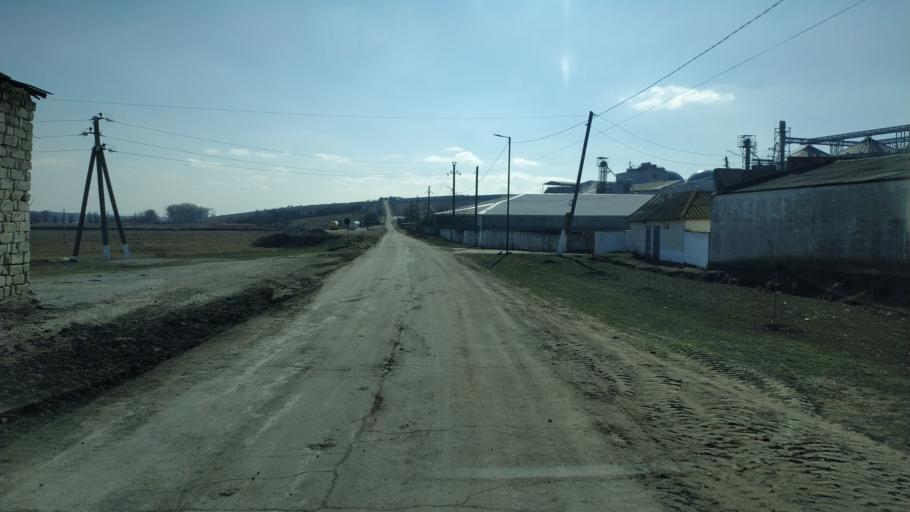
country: MD
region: Hincesti
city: Hincesti
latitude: 46.7827
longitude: 28.6805
